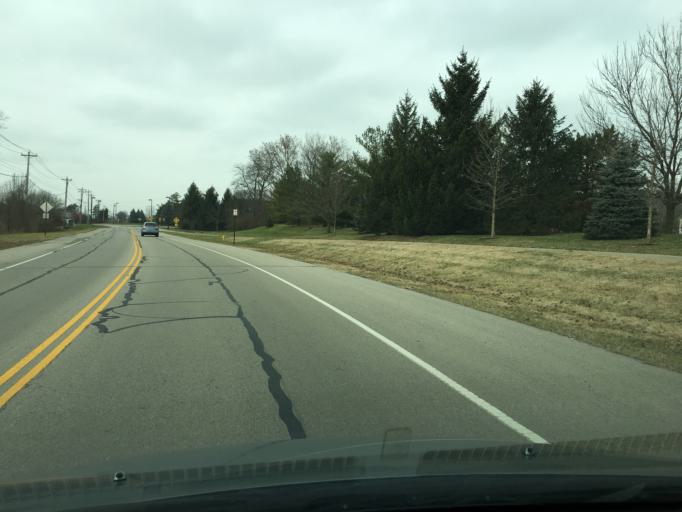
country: US
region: Ohio
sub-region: Butler County
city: Beckett Ridge
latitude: 39.3301
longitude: -84.4256
